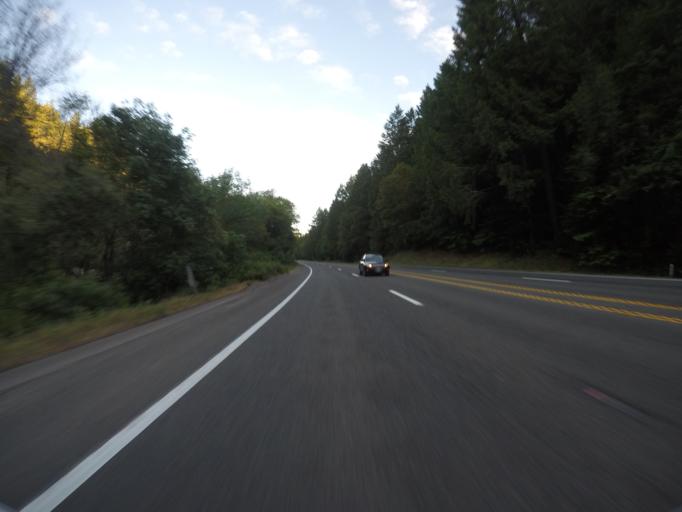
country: US
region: California
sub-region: Mendocino County
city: Laytonville
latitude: 39.5893
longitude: -123.4514
